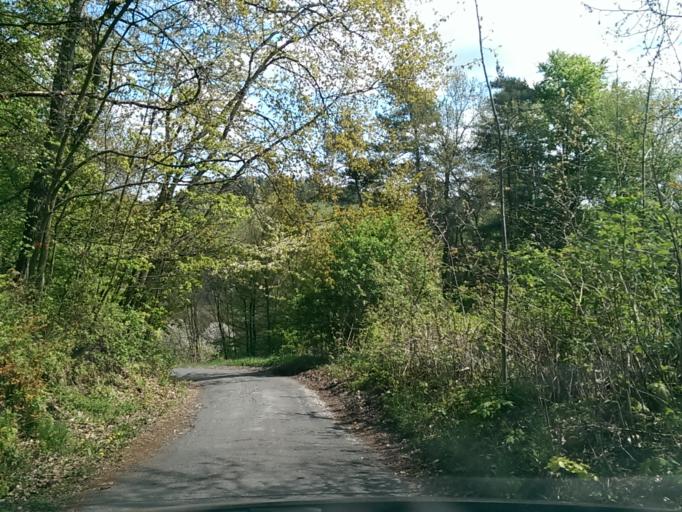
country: CZ
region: Liberecky
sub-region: Okres Semily
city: Turnov
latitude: 50.5520
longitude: 15.1407
